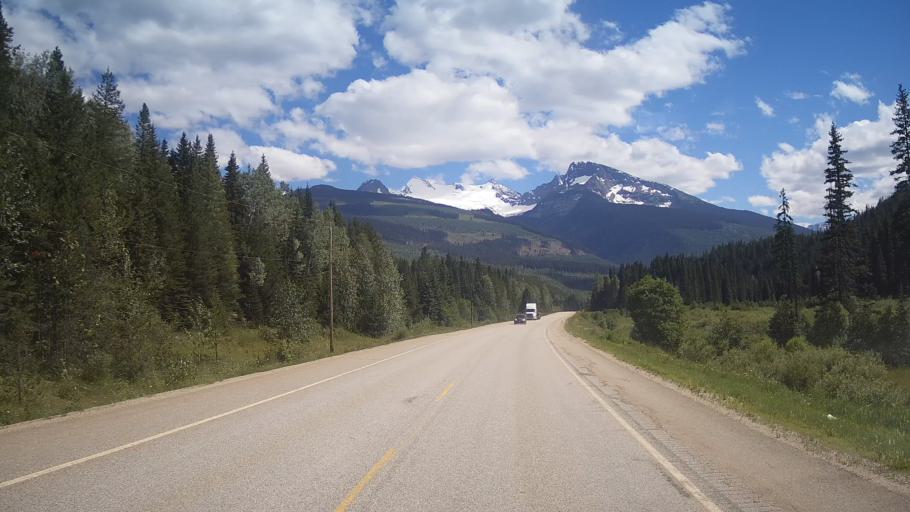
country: CA
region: Alberta
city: Jasper Park Lodge
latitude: 52.5945
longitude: -119.1017
